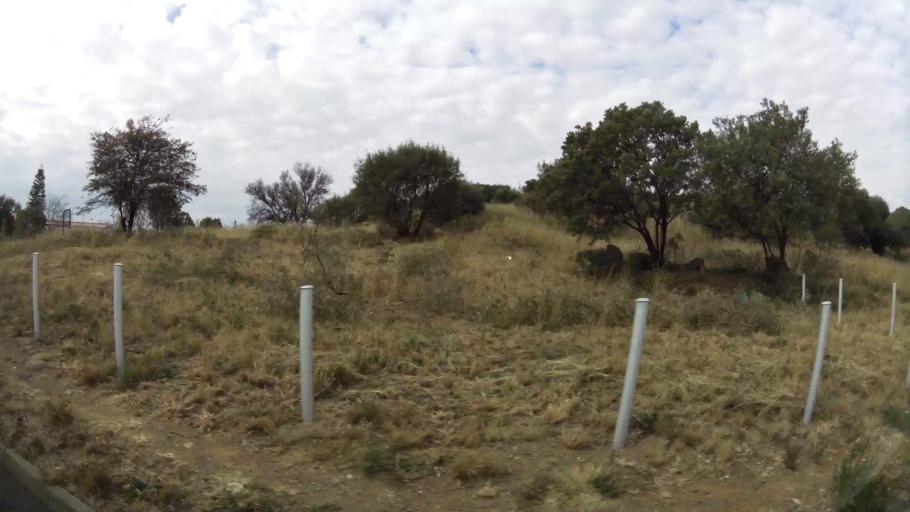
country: ZA
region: Orange Free State
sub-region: Mangaung Metropolitan Municipality
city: Bloemfontein
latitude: -29.0985
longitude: 26.2125
